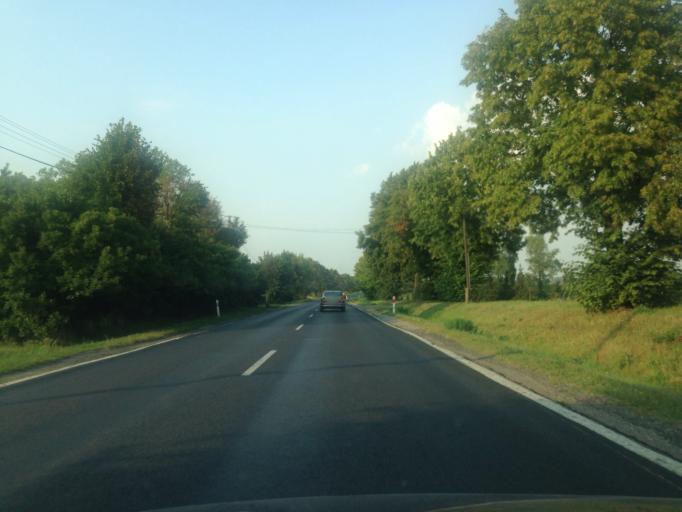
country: PL
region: Kujawsko-Pomorskie
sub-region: Powiat lipnowski
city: Lipno
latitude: 52.8157
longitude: 19.1447
